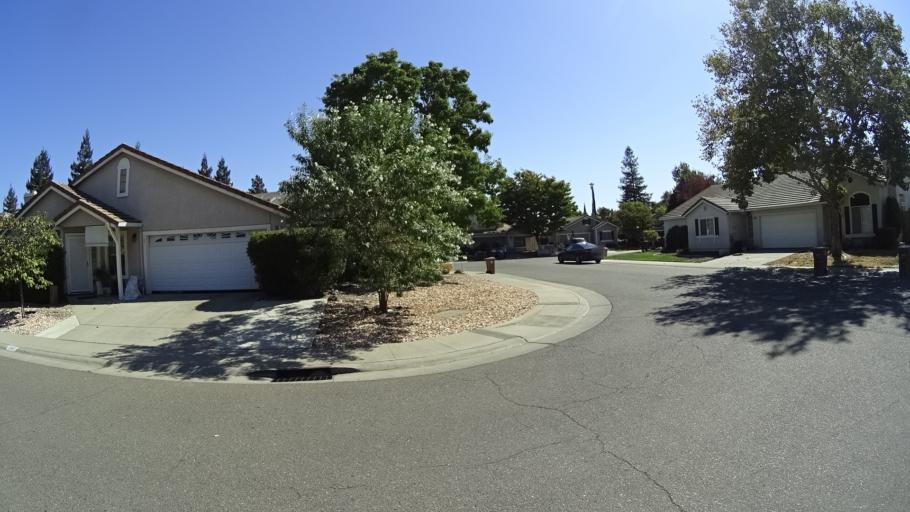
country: US
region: California
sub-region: Sacramento County
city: Laguna
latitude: 38.4256
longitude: -121.4217
